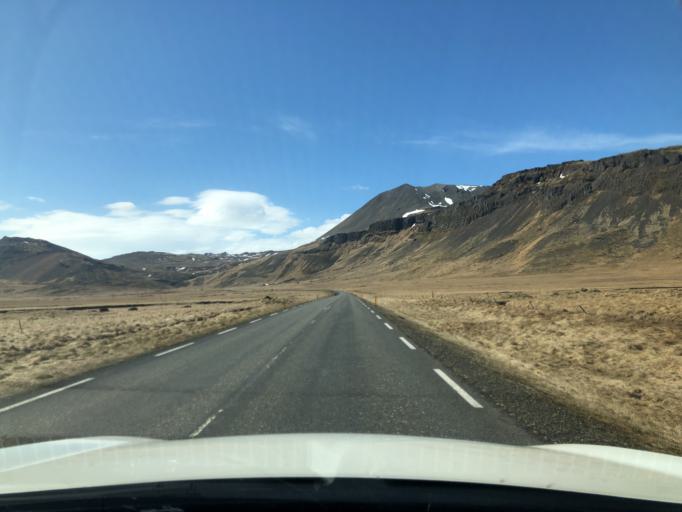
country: IS
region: West
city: Olafsvik
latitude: 64.8441
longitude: -23.3596
